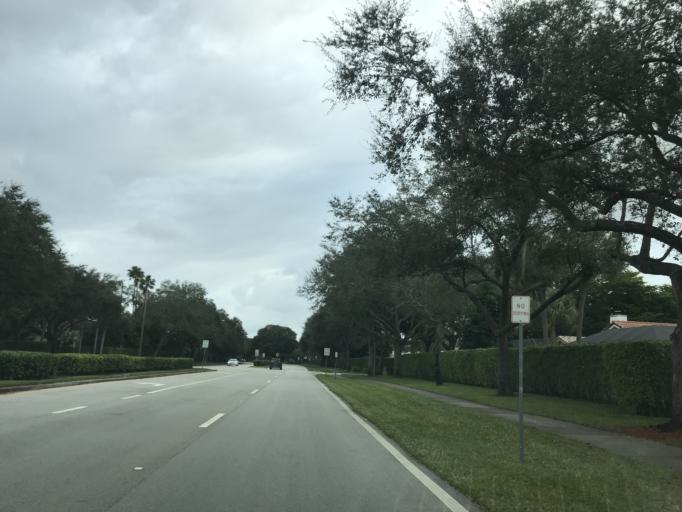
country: US
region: Florida
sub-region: Broward County
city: Parkland
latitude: 26.2988
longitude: -80.2437
